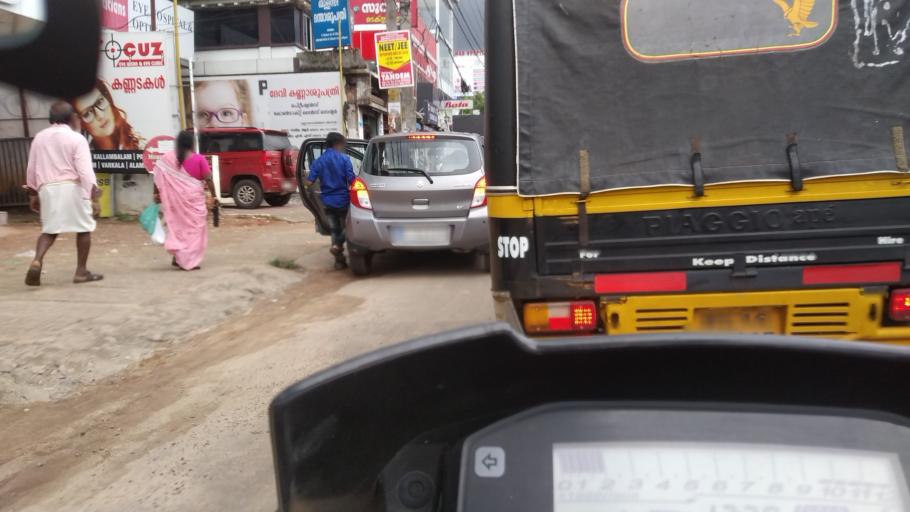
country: IN
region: Kerala
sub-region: Thiruvananthapuram
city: Attingal
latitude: 8.6990
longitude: 76.8136
